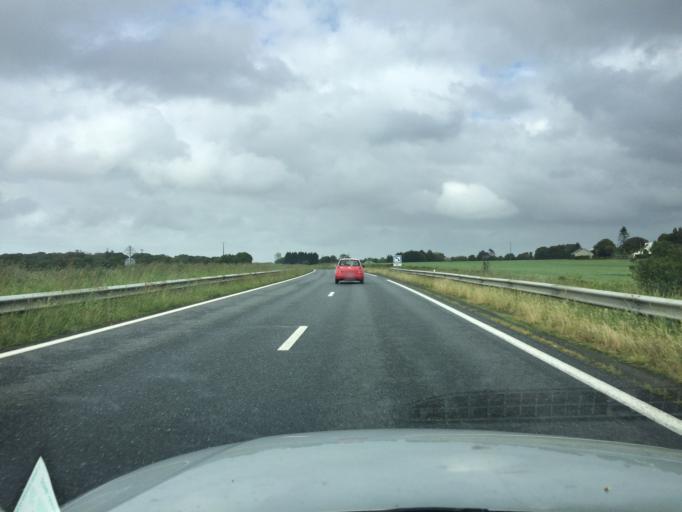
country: FR
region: Brittany
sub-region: Departement du Finistere
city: Guiclan
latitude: 48.5209
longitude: -3.9977
